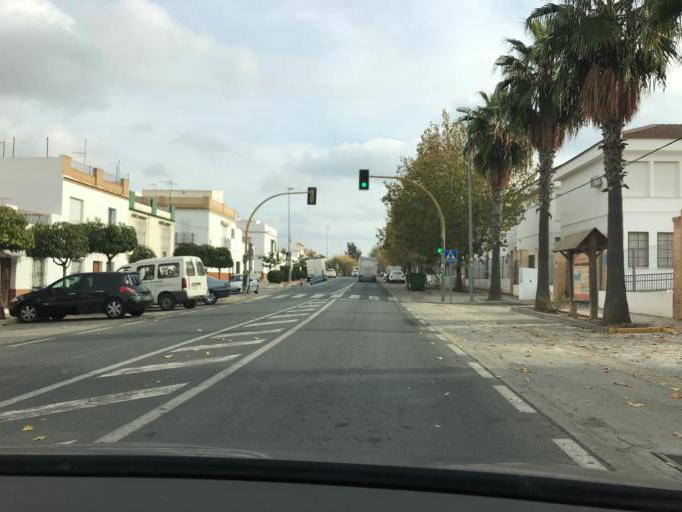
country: ES
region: Andalusia
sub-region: Provincia de Sevilla
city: La Campana
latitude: 37.5665
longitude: -5.4281
